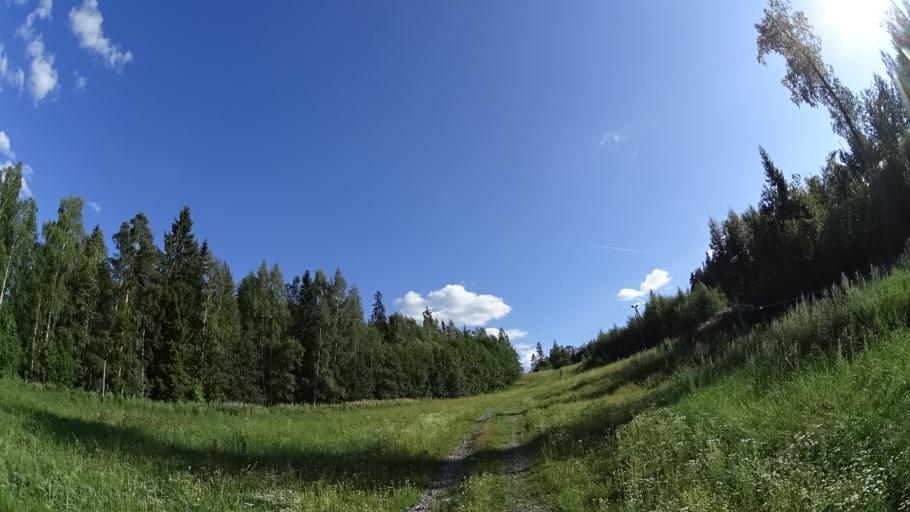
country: FI
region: Uusimaa
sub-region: Helsinki
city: Vihti
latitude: 60.3782
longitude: 24.3707
